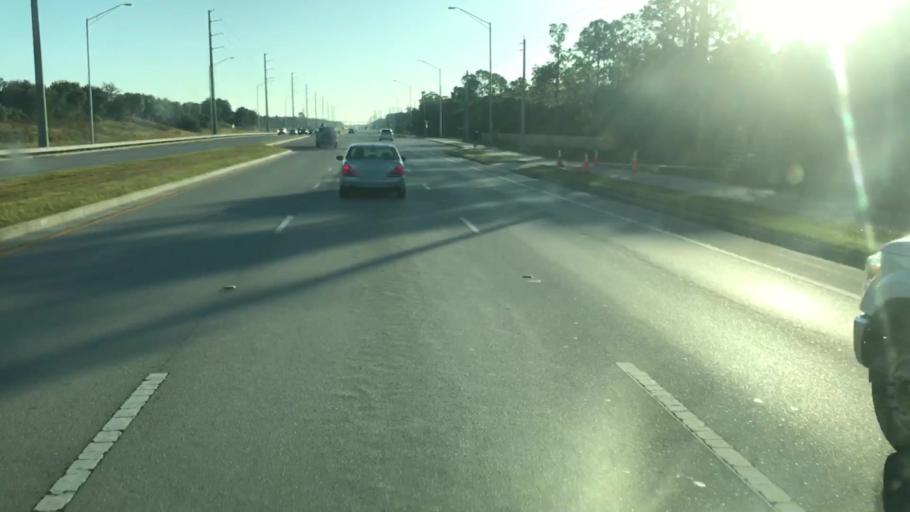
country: US
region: Florida
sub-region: Collier County
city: Orangetree
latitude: 26.2748
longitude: -81.6313
